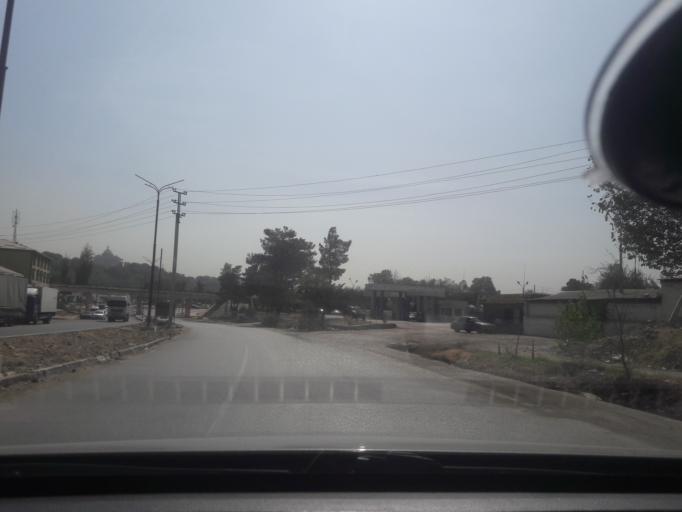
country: TJ
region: Dushanbe
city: Dushanbe
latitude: 38.6041
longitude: 68.7731
